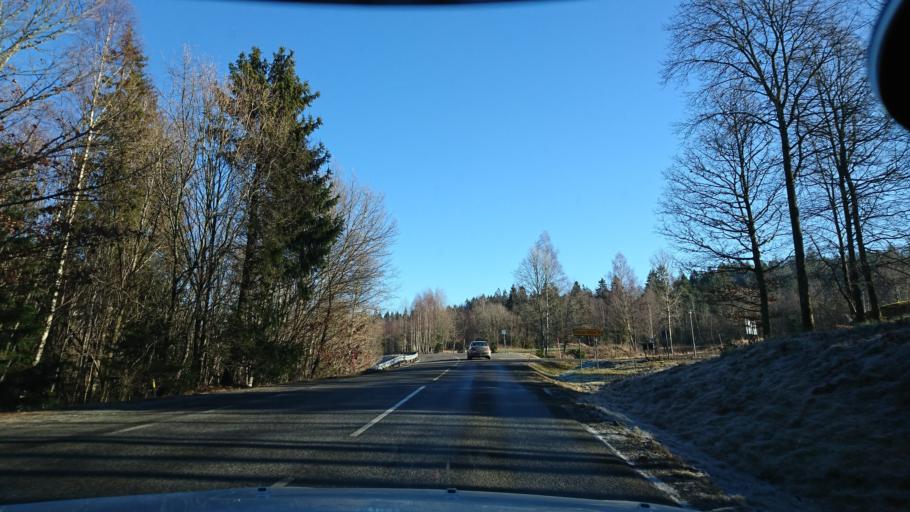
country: SE
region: Vaestra Goetaland
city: Svanesund
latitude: 58.1506
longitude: 11.8807
